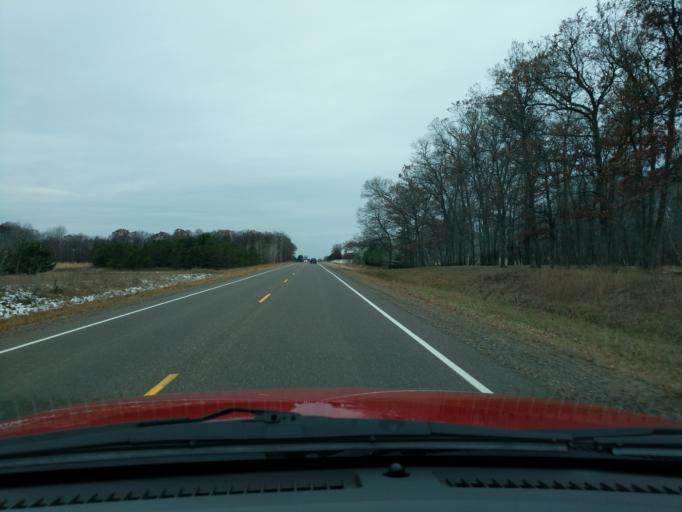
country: US
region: Wisconsin
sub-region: Burnett County
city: Siren
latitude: 45.8088
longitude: -92.1630
